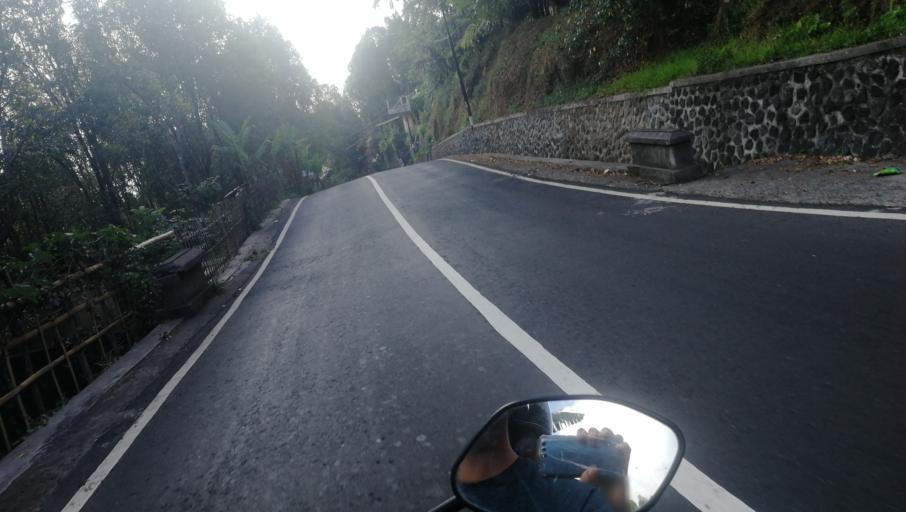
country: ID
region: Bali
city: Munduk
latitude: -8.2617
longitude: 115.0687
